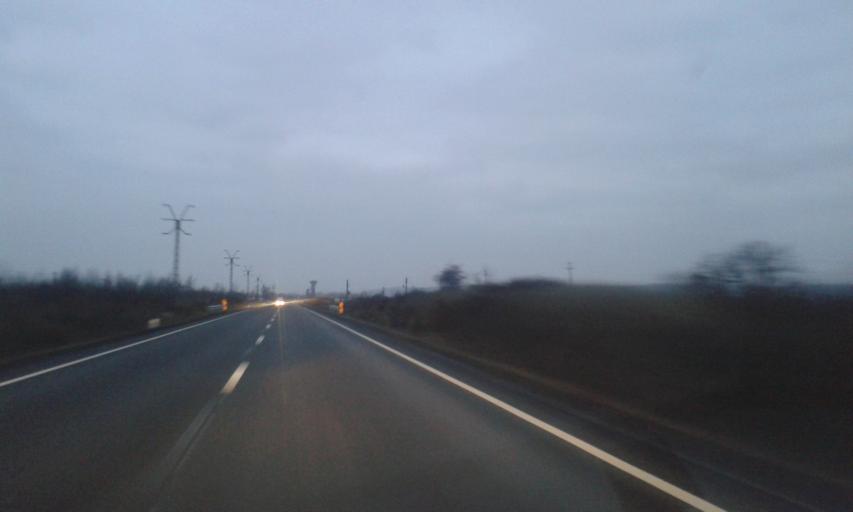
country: RO
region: Gorj
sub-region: Comuna Turcinesti
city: Turcinesti
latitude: 45.1202
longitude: 23.3515
